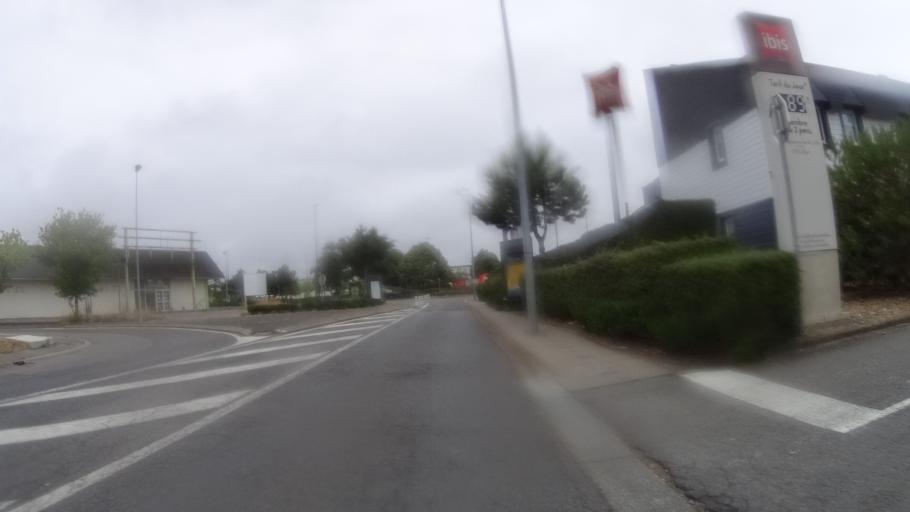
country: FR
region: Pays de la Loire
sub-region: Departement de la Loire-Atlantique
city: Saint-Nazaire
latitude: 47.3001
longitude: -2.2088
